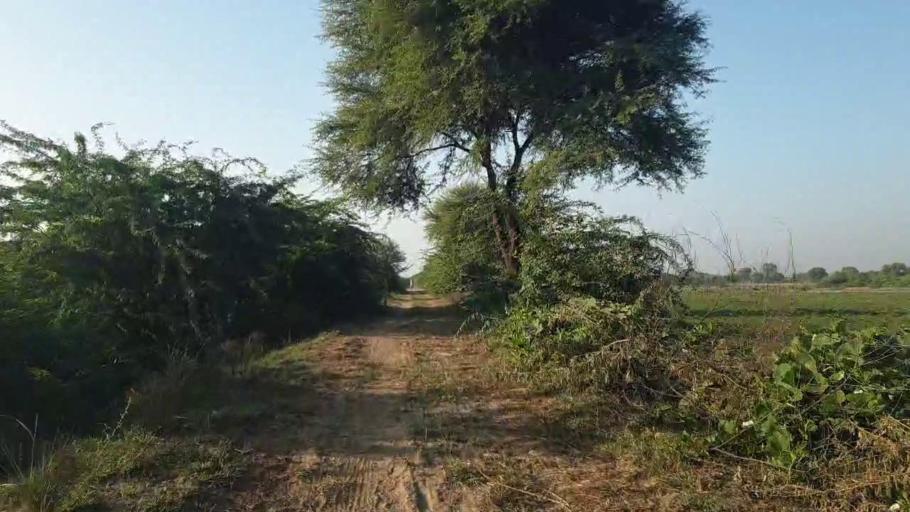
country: PK
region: Sindh
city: Badin
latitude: 24.6091
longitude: 68.7827
